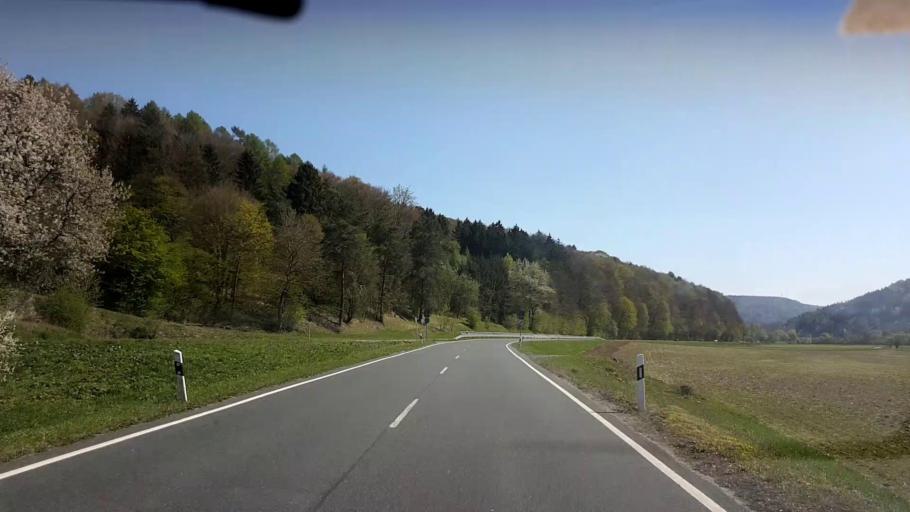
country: DE
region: Bavaria
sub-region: Upper Franconia
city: Unterleinleiter
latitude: 49.8154
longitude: 11.1935
